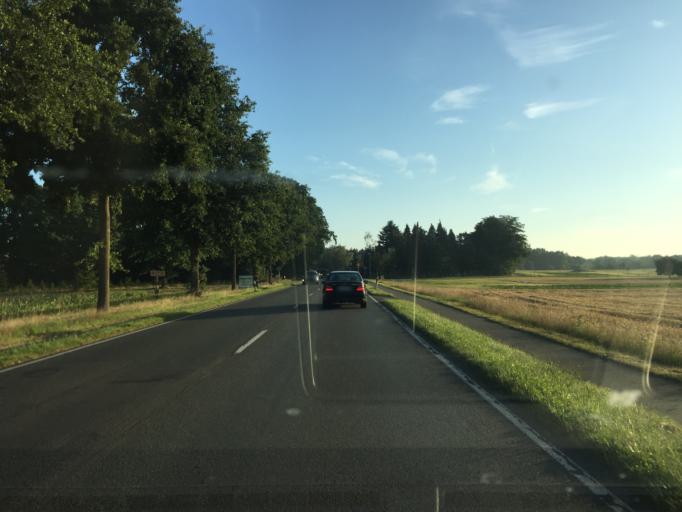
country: DE
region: Lower Saxony
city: Rohrsen
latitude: 52.6961
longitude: 9.2363
